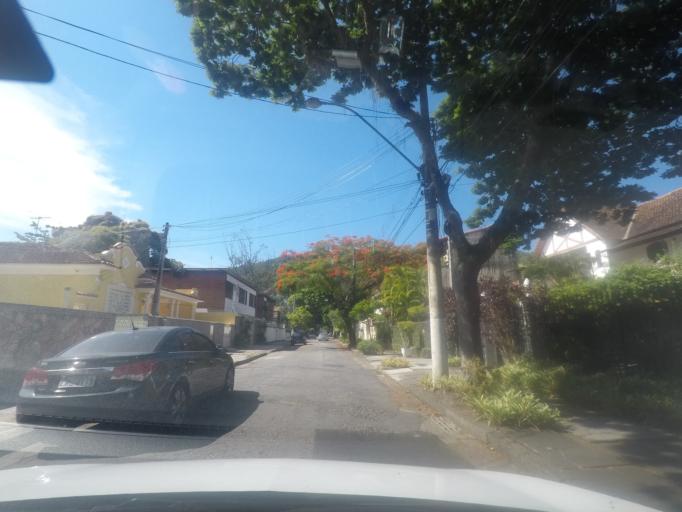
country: BR
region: Rio de Janeiro
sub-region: Niteroi
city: Niteroi
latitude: -22.9179
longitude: -43.0916
